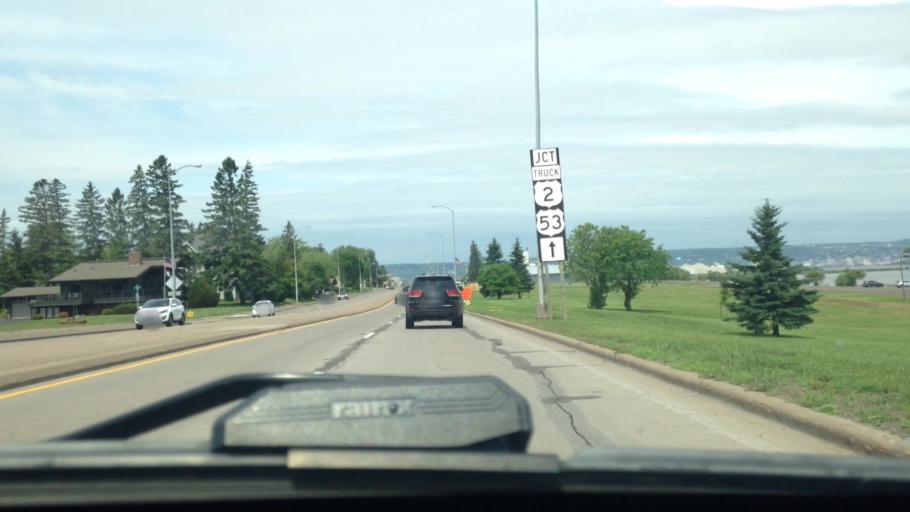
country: US
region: Wisconsin
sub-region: Douglas County
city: Superior
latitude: 46.7196
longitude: -92.0644
